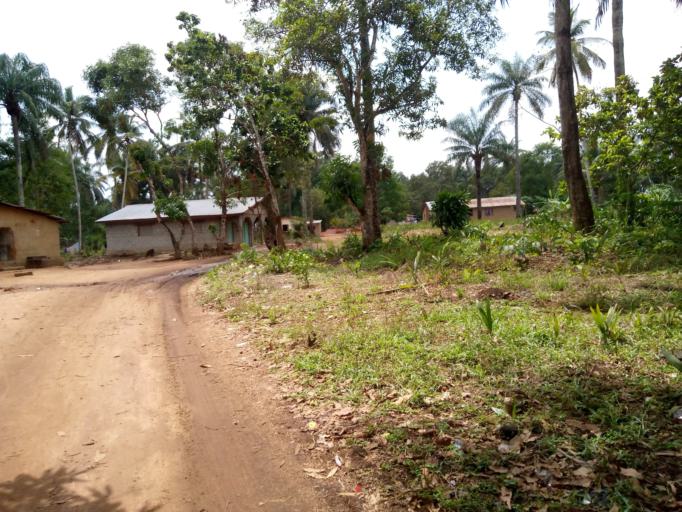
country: SL
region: Western Area
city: Waterloo
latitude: 8.3392
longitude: -13.0082
